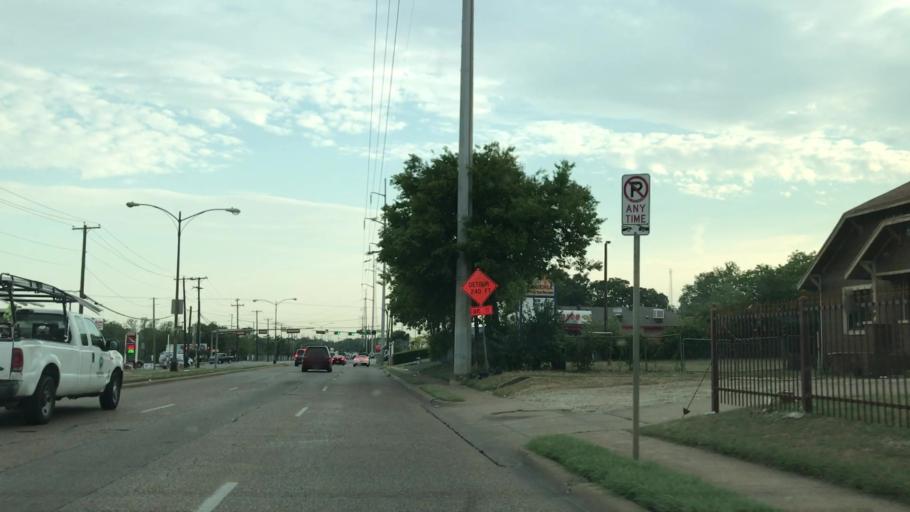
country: US
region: Texas
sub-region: Dallas County
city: Cockrell Hill
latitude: 32.7520
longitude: -96.8740
